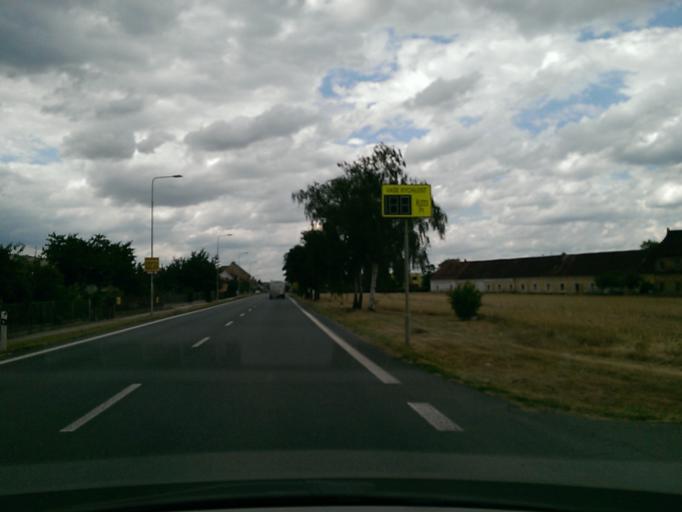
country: CZ
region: Central Bohemia
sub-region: Okres Nymburk
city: Nymburk
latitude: 50.2184
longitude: 15.0297
